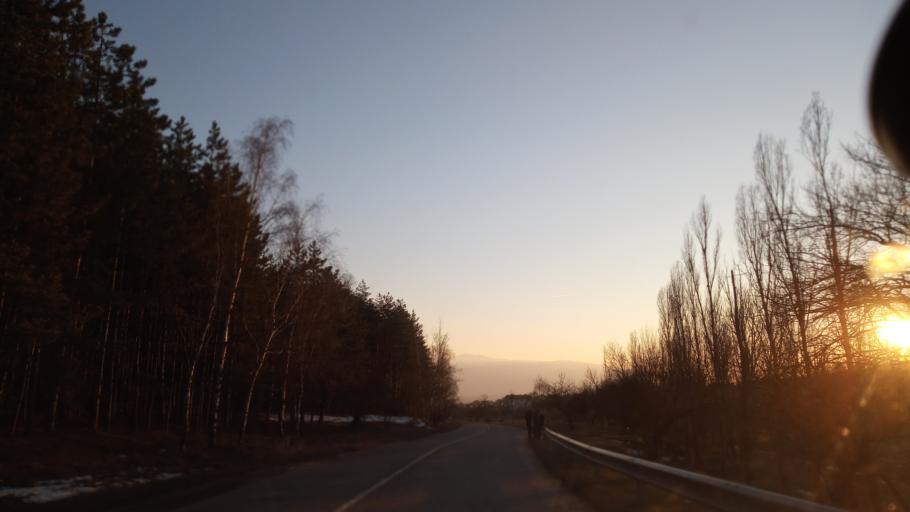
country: BG
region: Sofia-Capital
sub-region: Stolichna Obshtina
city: Bukhovo
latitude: 42.7868
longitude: 23.5216
